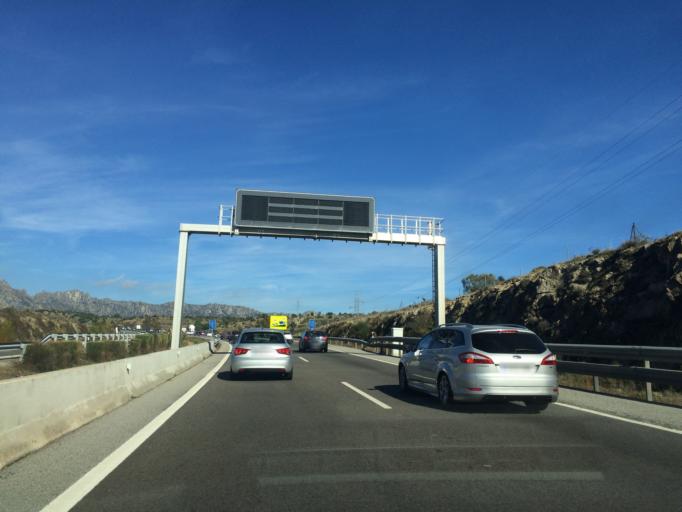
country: ES
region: Madrid
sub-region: Provincia de Madrid
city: Cabanillas de la Sierra
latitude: 40.8287
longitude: -3.6142
